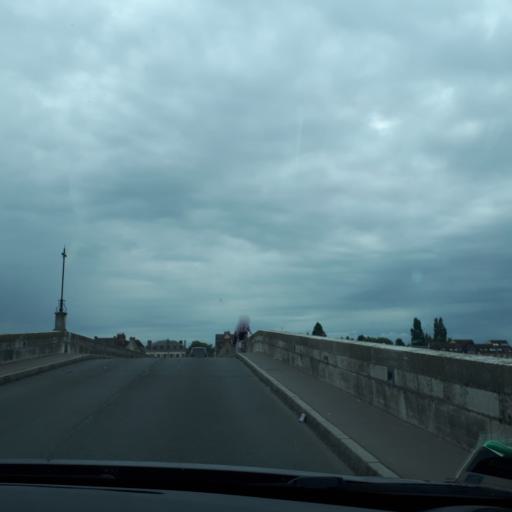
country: FR
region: Centre
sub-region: Departement du Loiret
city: Gien
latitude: 47.6829
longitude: 2.6311
